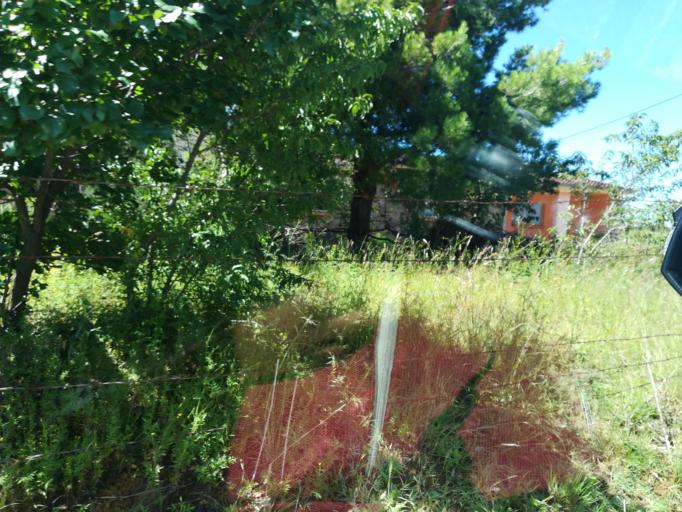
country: LS
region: Quthing
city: Quthing
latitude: -30.3298
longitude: 27.5317
